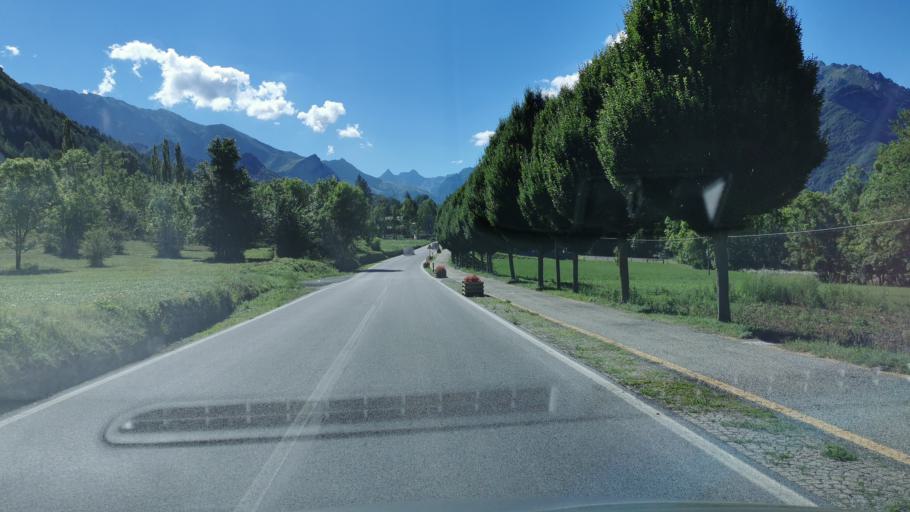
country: IT
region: Piedmont
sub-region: Provincia di Cuneo
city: Entracque
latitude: 44.2481
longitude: 7.3924
